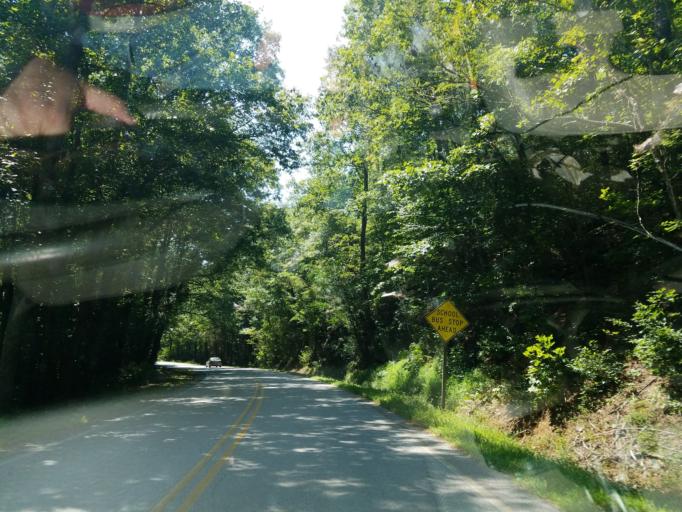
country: US
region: Georgia
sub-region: Lumpkin County
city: Dahlonega
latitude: 34.6353
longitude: -83.9325
